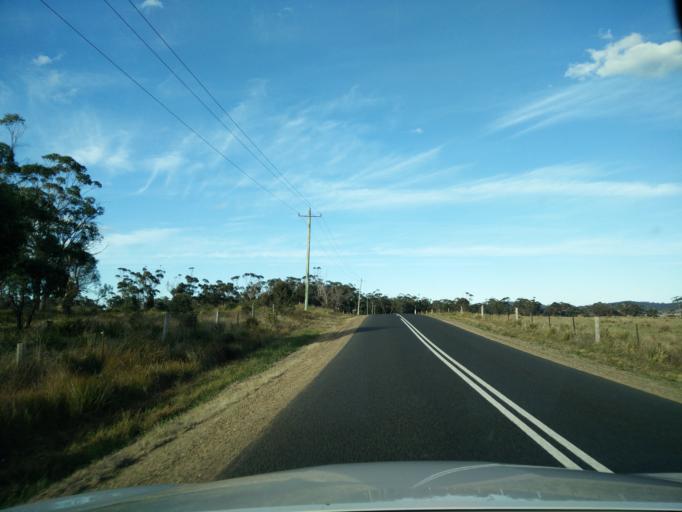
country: AU
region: Tasmania
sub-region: Break O'Day
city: St Helens
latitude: -41.9208
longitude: 148.2422
